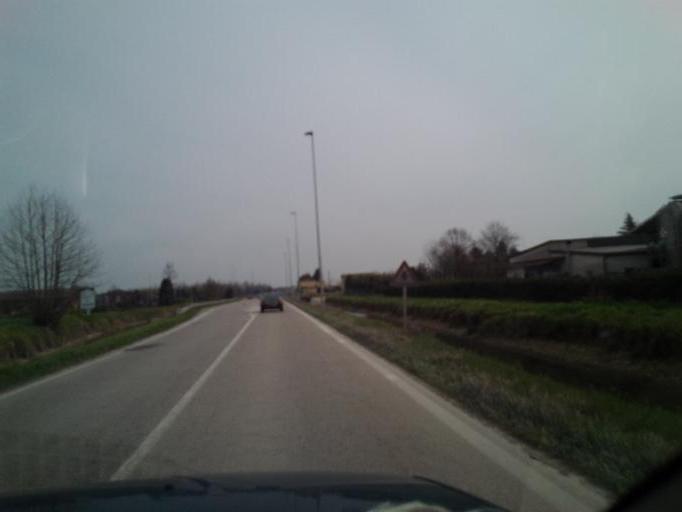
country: IT
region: Lombardy
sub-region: Provincia di Mantova
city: Roverbella
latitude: 45.2601
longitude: 10.7506
